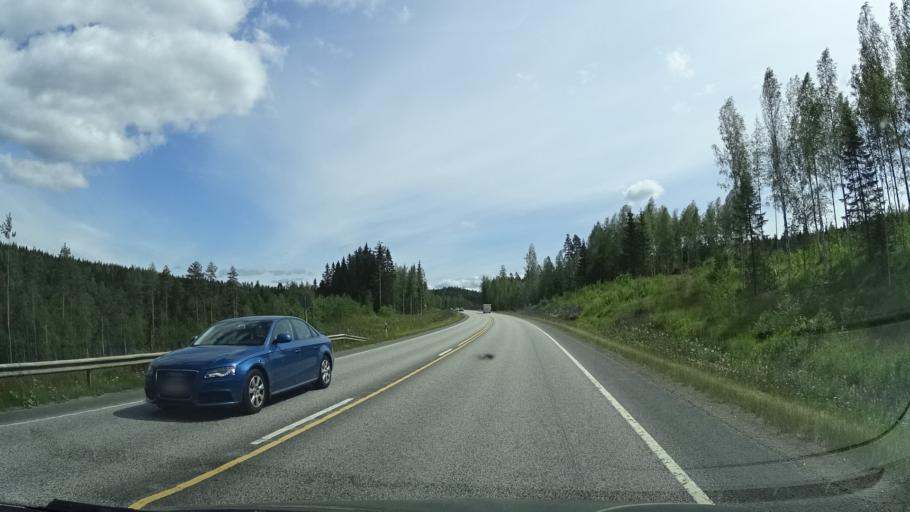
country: FI
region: Central Finland
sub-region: Jyvaeskylae
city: Jyvaeskylae
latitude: 62.2540
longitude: 25.6288
